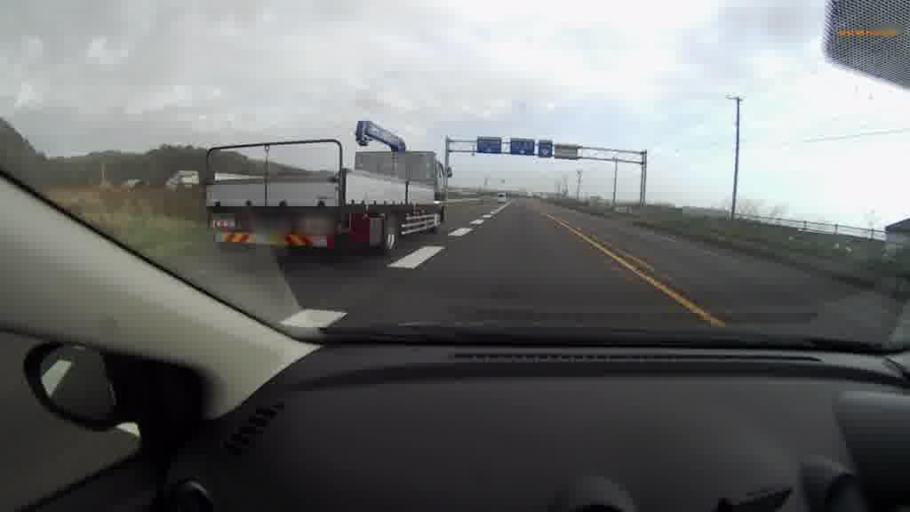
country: JP
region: Hokkaido
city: Kushiro
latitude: 42.9654
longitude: 144.1160
